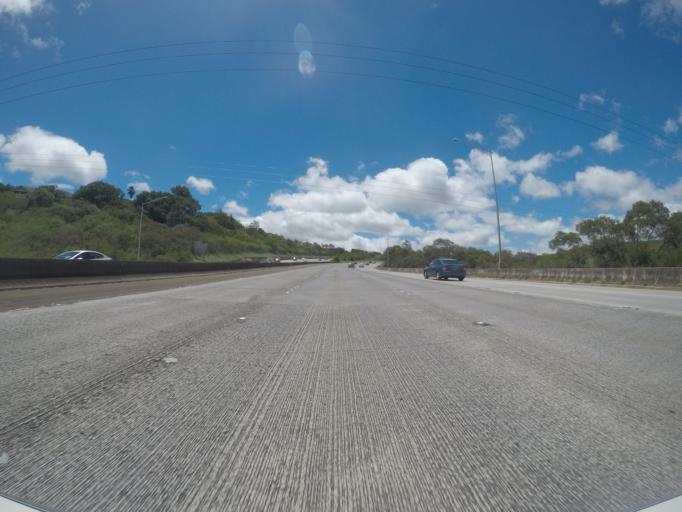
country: US
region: Hawaii
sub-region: Honolulu County
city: Waipio
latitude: 21.4151
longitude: -157.9920
